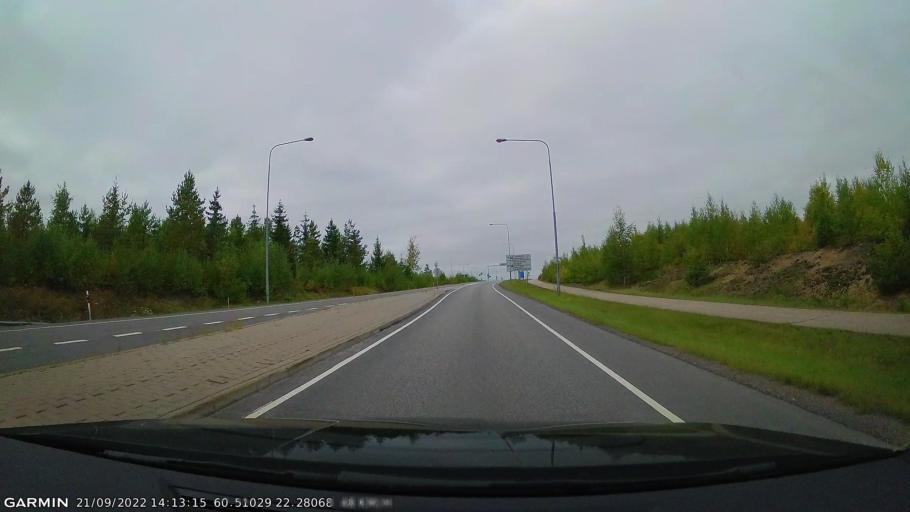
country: FI
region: Varsinais-Suomi
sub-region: Turku
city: Turku
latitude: 60.5100
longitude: 22.2816
